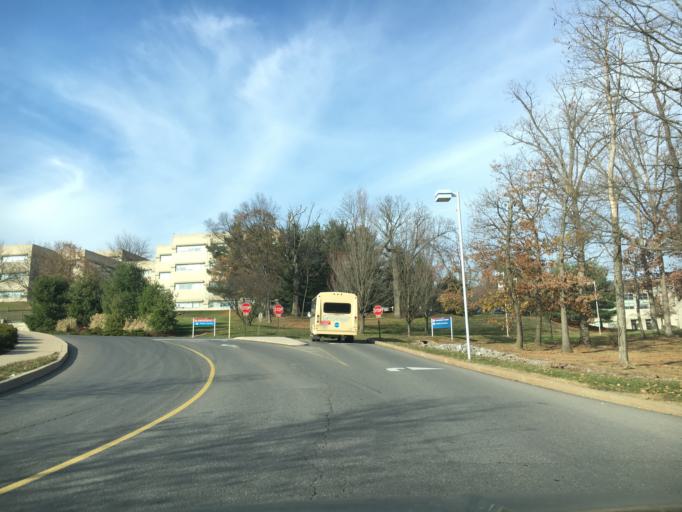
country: US
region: Pennsylvania
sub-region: Montour County
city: Danville
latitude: 40.9695
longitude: -76.6016
